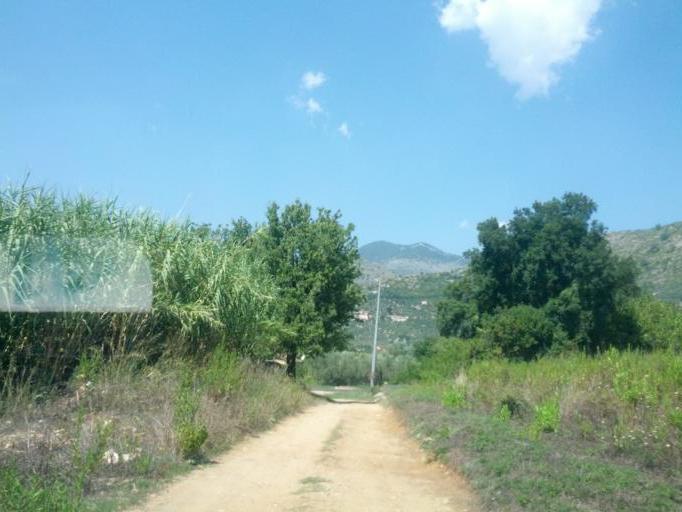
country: IT
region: Latium
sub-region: Provincia di Latina
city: Monte San Biagio
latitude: 41.3671
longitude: 13.3539
